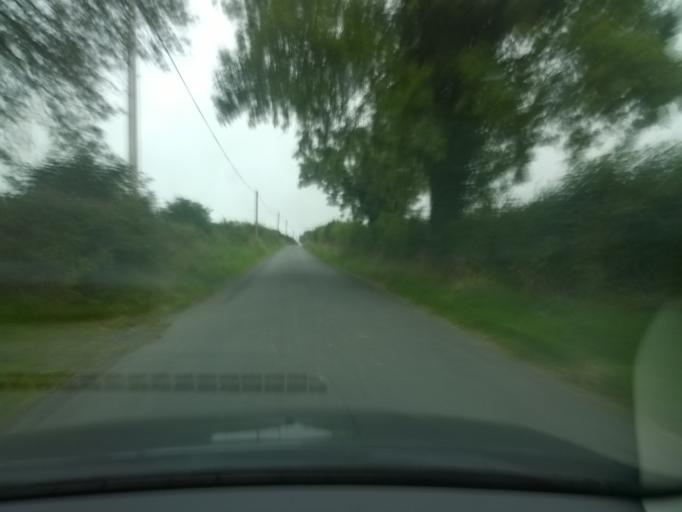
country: IE
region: Leinster
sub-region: Kildare
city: Cherryville
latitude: 53.1788
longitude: -6.9420
